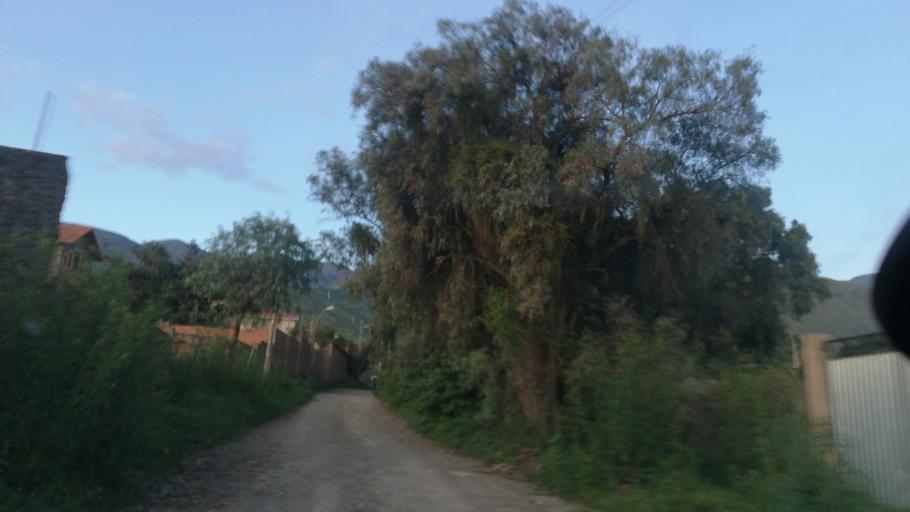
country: BO
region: Cochabamba
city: Cochabamba
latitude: -17.3331
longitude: -66.2081
